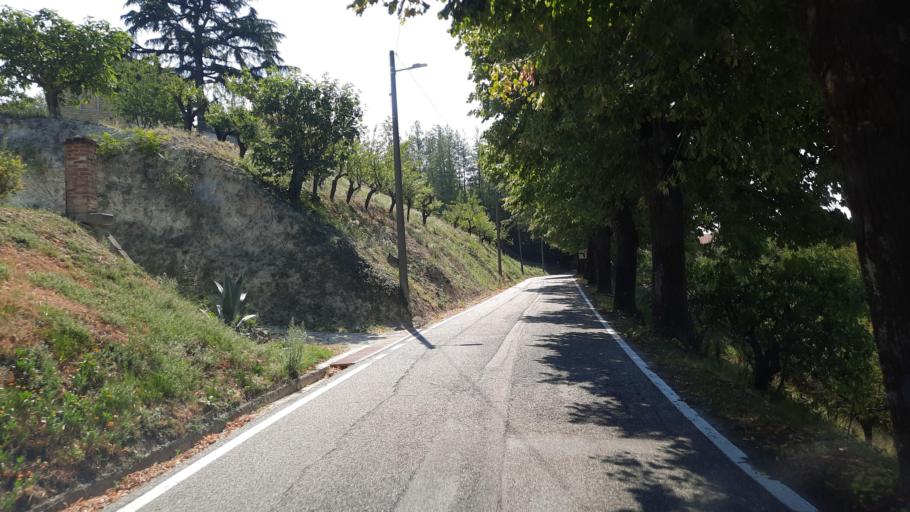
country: IT
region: Piedmont
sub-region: Provincia di Alessandria
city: Mombello Monferrato
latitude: 45.1555
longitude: 8.2321
